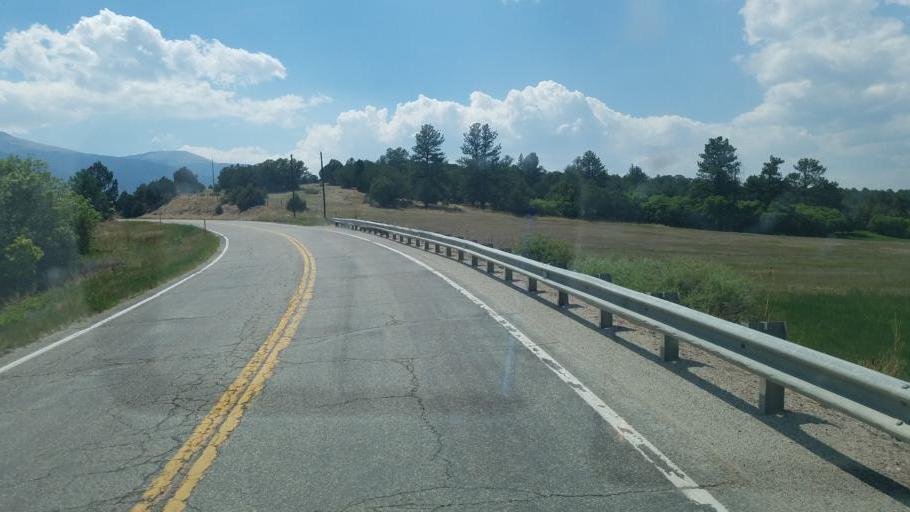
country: US
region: Colorado
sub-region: Custer County
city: Westcliffe
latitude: 38.2636
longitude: -105.6020
